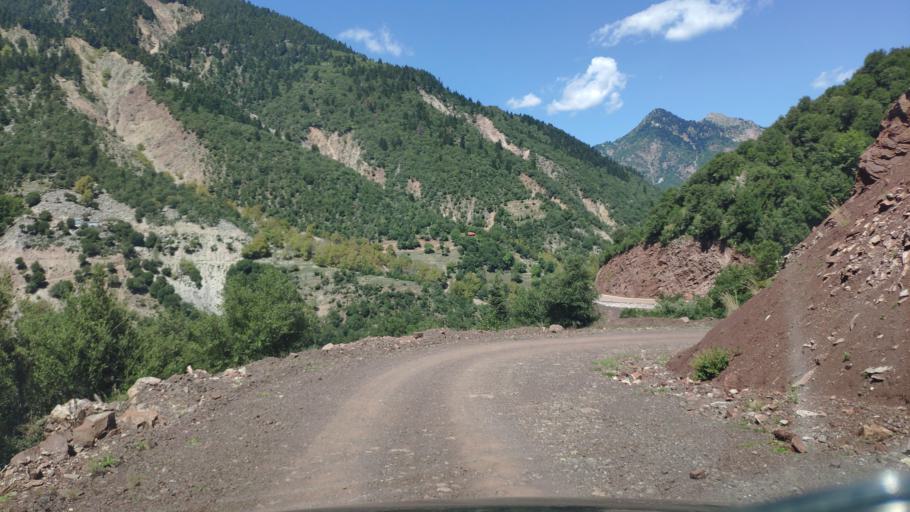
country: GR
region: Central Greece
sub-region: Nomos Evrytanias
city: Kerasochori
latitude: 39.1253
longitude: 21.6275
